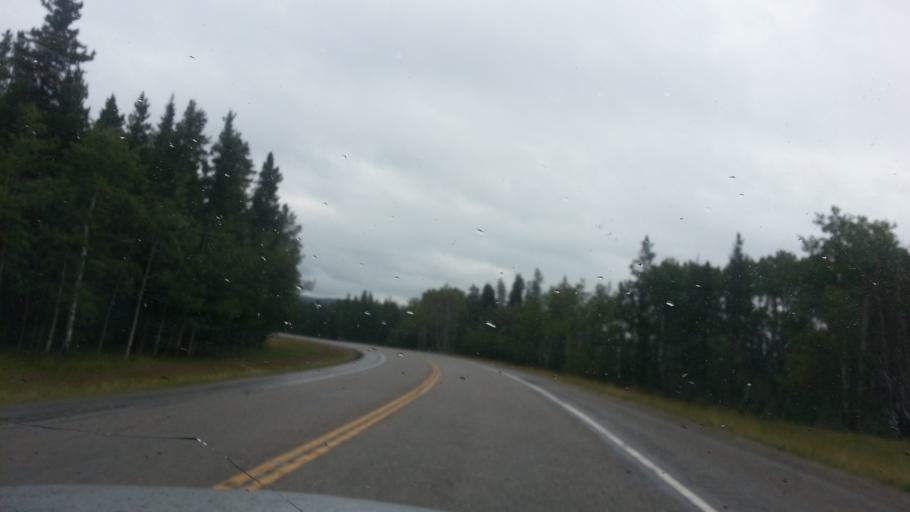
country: CA
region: Alberta
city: Cochrane
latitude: 50.8876
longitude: -114.7065
